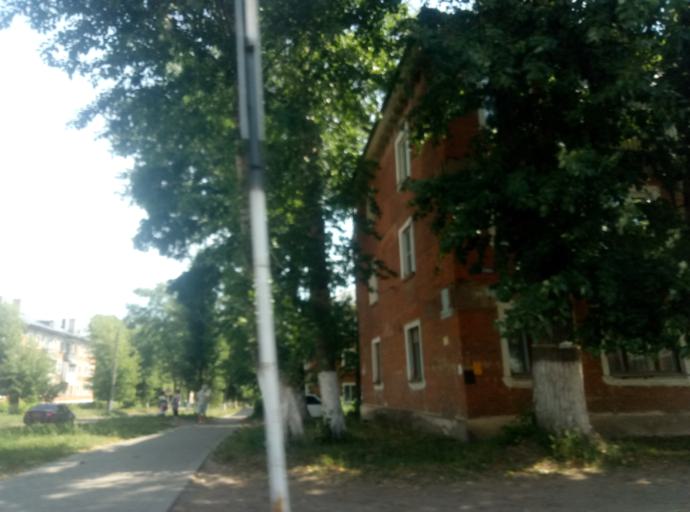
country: RU
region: Tula
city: Kireyevsk
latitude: 53.9283
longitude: 37.9339
